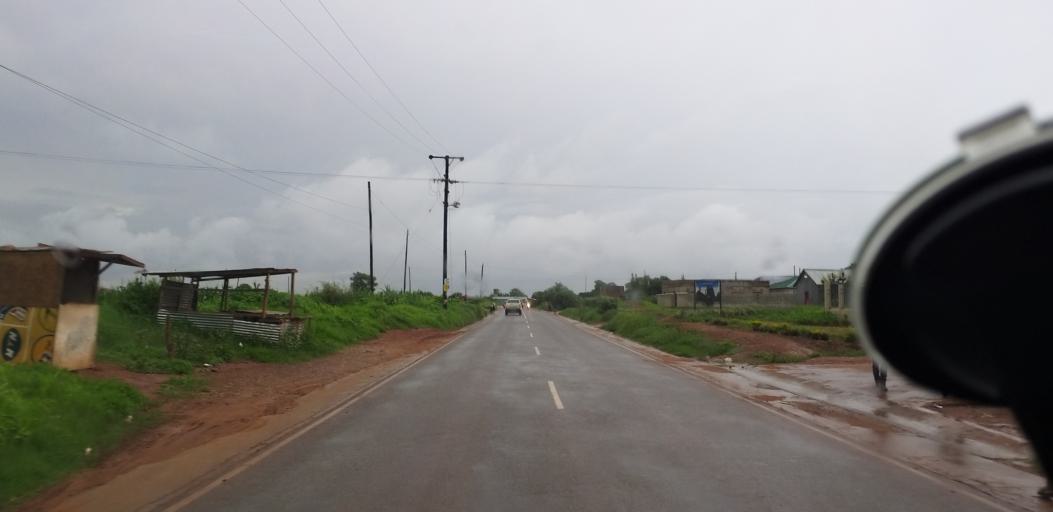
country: ZM
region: Lusaka
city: Lusaka
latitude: -15.5179
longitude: 28.2977
